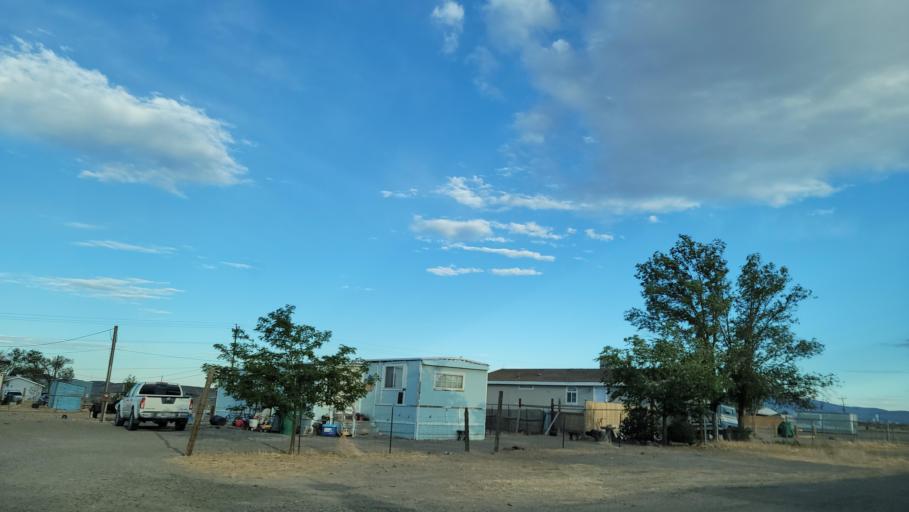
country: US
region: Nevada
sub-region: Lyon County
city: Silver Springs
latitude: 39.4050
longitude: -119.2216
